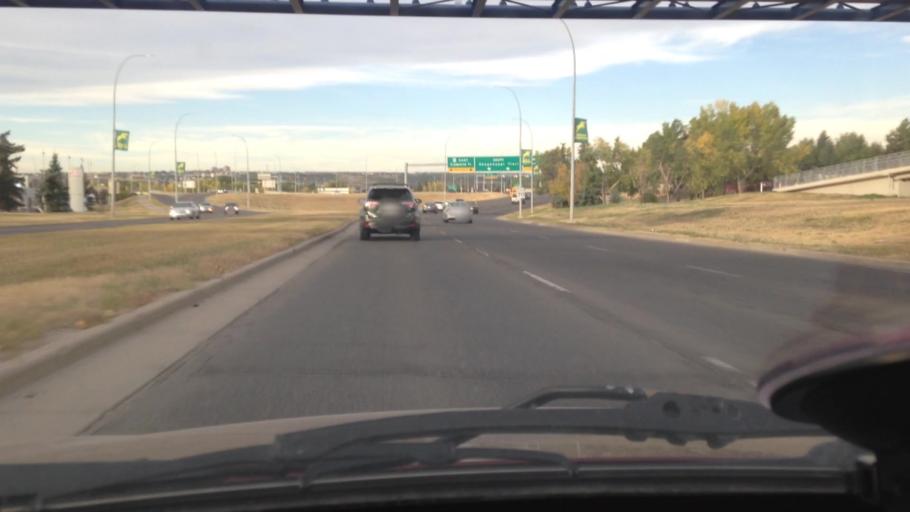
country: CA
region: Alberta
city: Calgary
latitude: 51.1008
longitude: -114.1455
